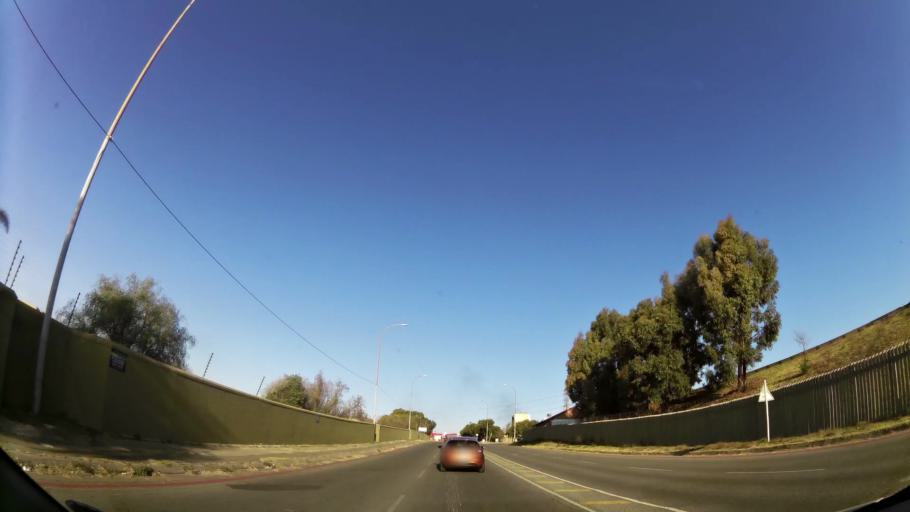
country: ZA
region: Gauteng
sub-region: City of Johannesburg Metropolitan Municipality
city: Roodepoort
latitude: -26.1366
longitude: 27.8633
